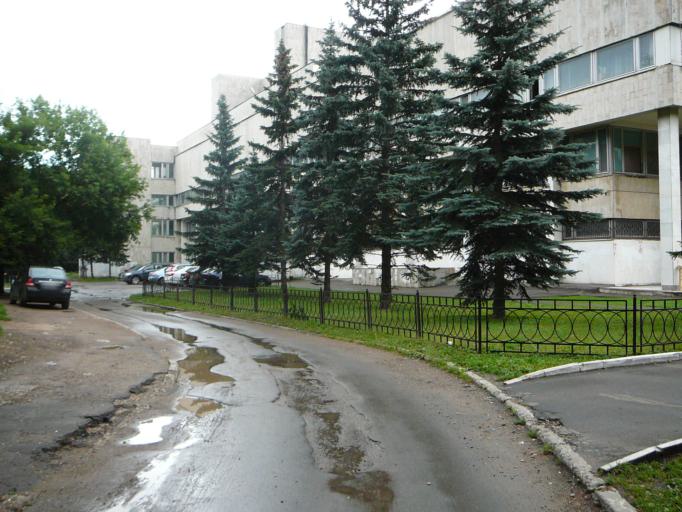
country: RU
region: Moskovskaya
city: Krasnogorsk
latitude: 55.8246
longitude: 37.3197
